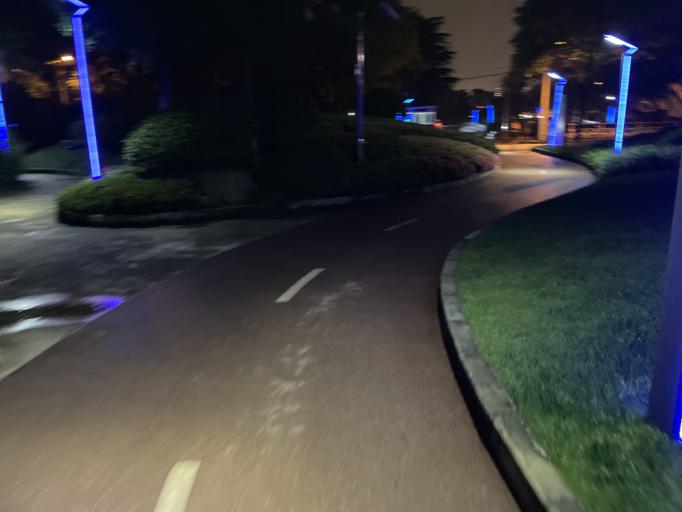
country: CN
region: Shanghai Shi
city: Changqiao
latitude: 31.1545
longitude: 121.4027
